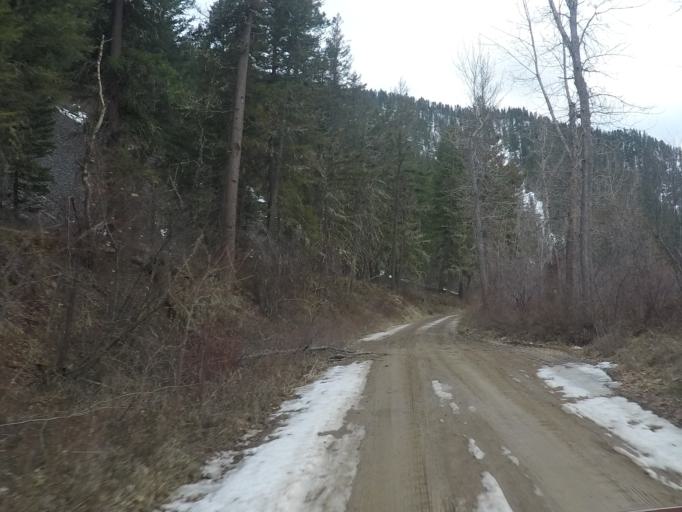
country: US
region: Montana
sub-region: Missoula County
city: Clinton
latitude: 46.5729
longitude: -113.6850
